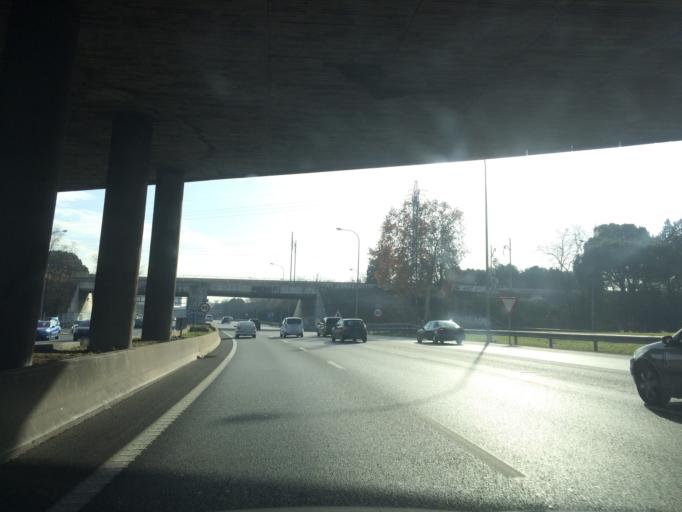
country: ES
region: Madrid
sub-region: Provincia de Madrid
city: Moncloa-Aravaca
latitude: 40.4350
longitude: -3.7383
